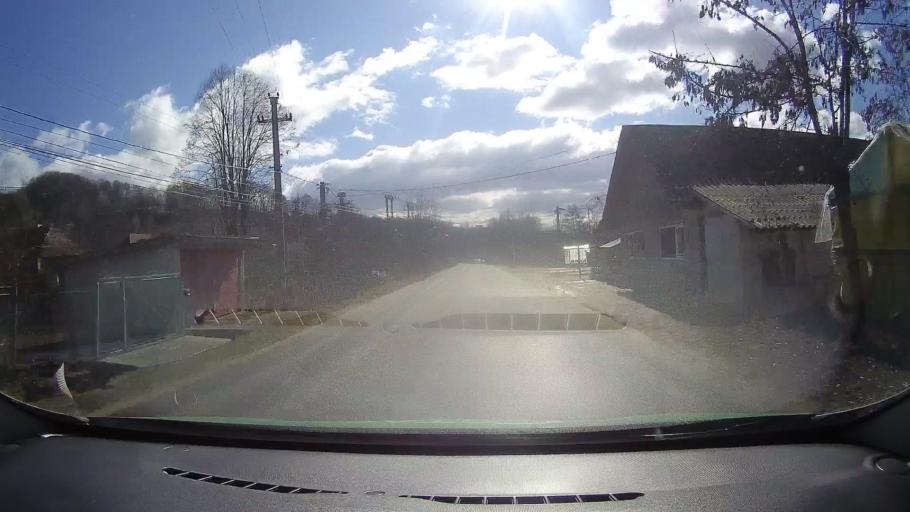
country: RO
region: Dambovita
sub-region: Comuna Runcu
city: Badeni
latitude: 45.1511
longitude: 25.4015
